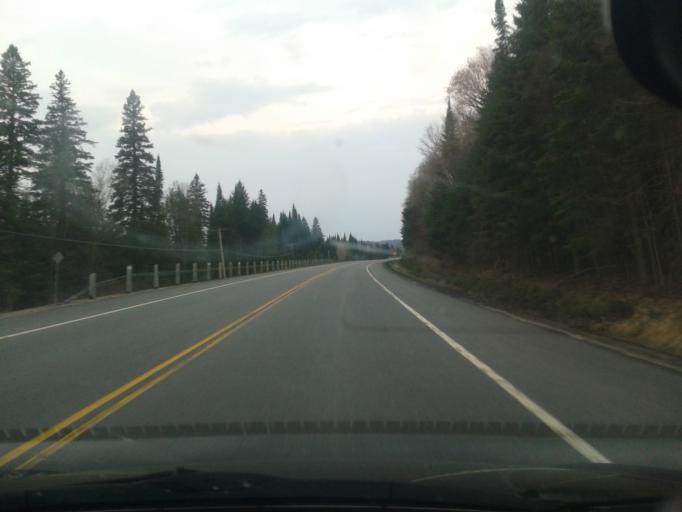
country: CA
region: Ontario
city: Huntsville
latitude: 45.4977
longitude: -78.7451
